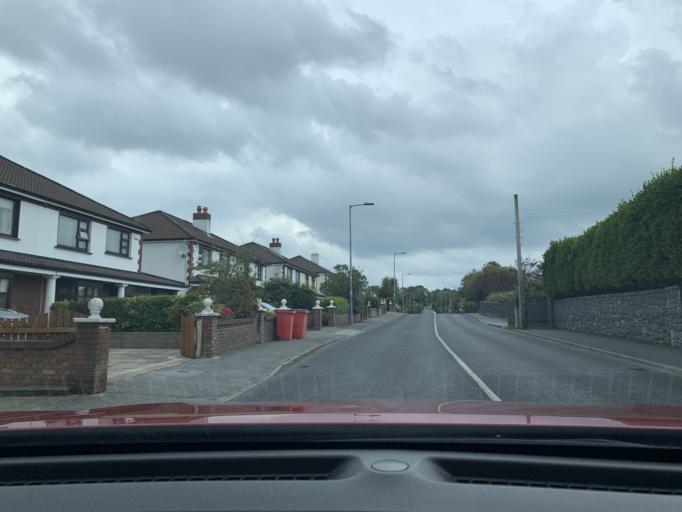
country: IE
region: Connaught
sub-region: County Galway
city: Bearna
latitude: 53.2642
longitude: -9.1172
